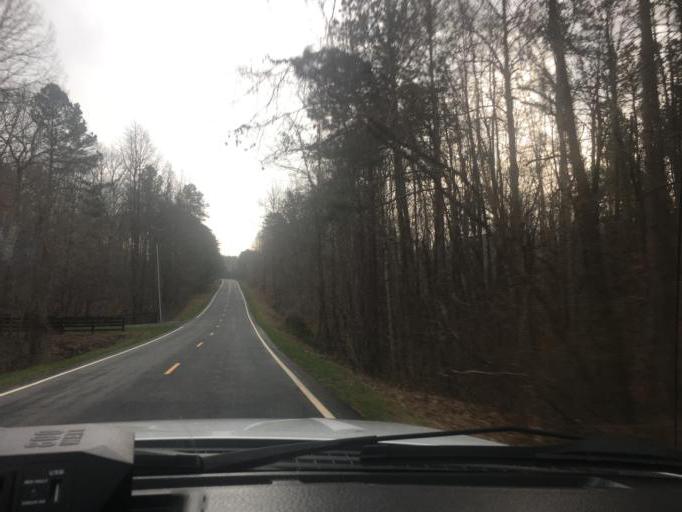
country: US
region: Georgia
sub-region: Dawson County
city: Dawsonville
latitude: 34.3511
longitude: -84.2063
